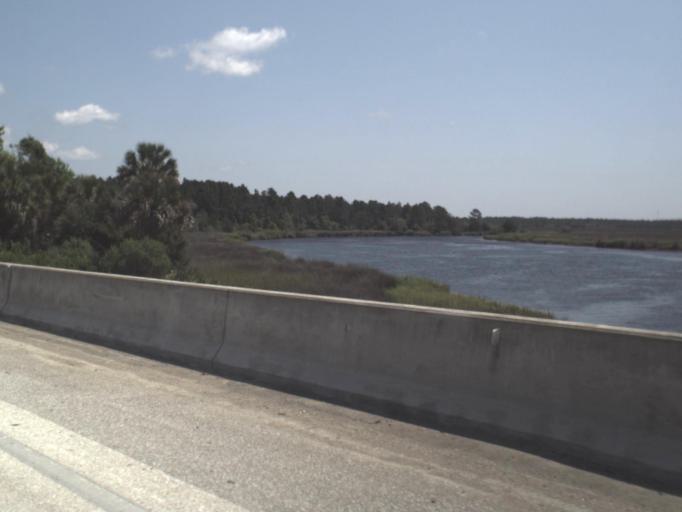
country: US
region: Florida
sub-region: Nassau County
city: Yulee
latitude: 30.5761
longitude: -81.6458
